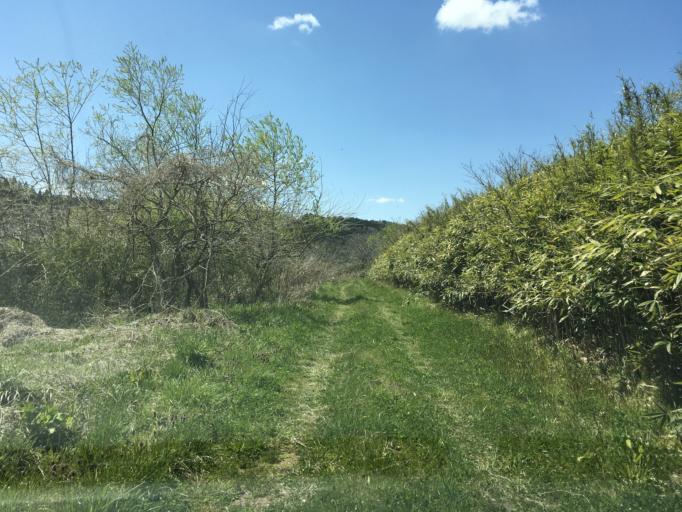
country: JP
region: Iwate
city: Ichinoseki
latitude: 38.8301
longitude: 141.2577
